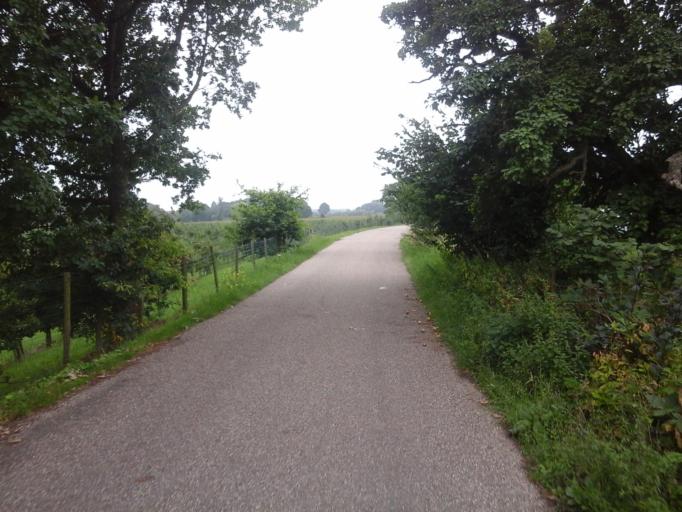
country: NL
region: Gelderland
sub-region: Gemeente Geldermalsen
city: Geldermalsen
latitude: 51.8859
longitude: 5.2638
